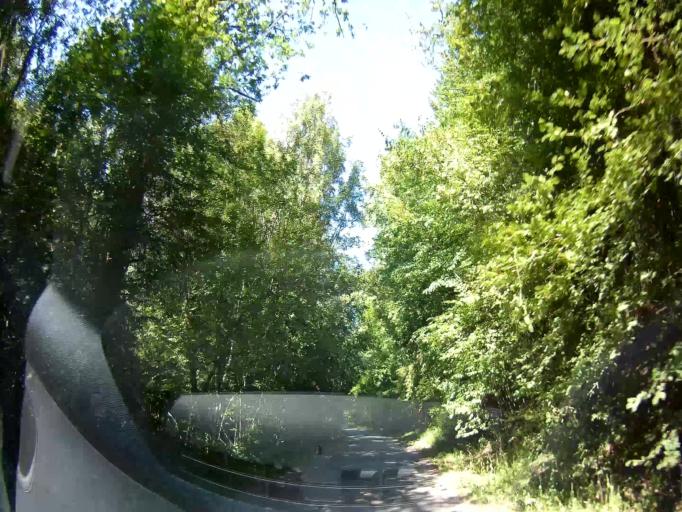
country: BE
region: Wallonia
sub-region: Province de Namur
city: Houyet
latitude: 50.2270
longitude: 4.9812
